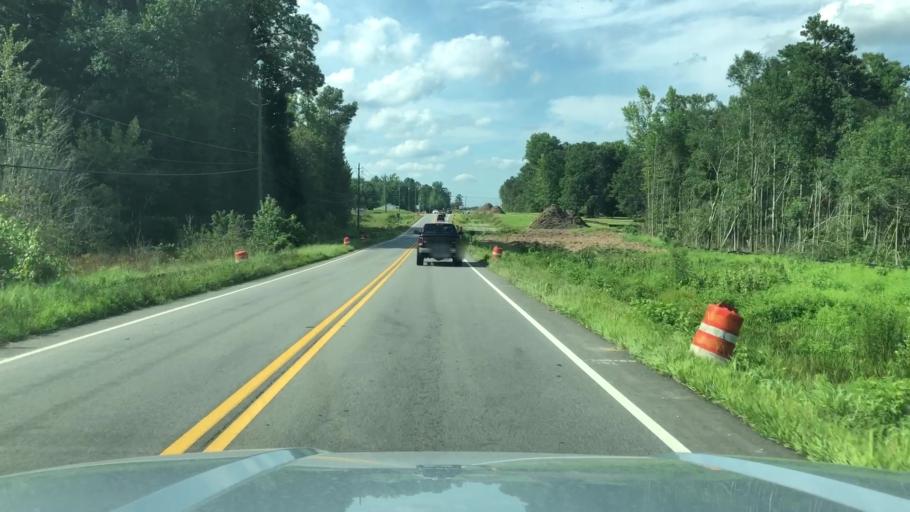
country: US
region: Georgia
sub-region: Paulding County
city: Hiram
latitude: 33.8290
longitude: -84.7592
